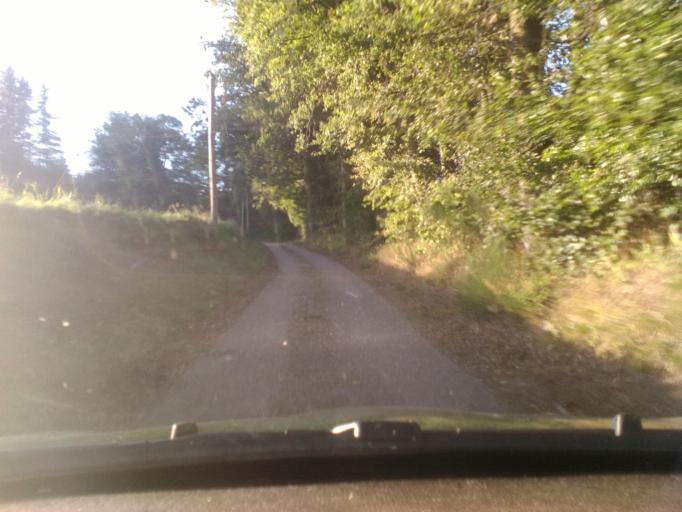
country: FR
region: Lorraine
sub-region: Departement des Vosges
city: Senones
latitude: 48.3728
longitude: 7.0341
